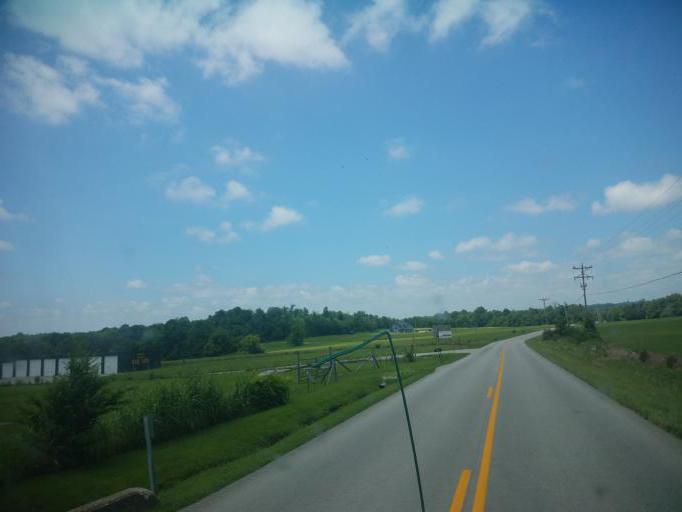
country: US
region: Kentucky
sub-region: Edmonson County
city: Brownsville
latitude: 37.3270
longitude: -86.1211
